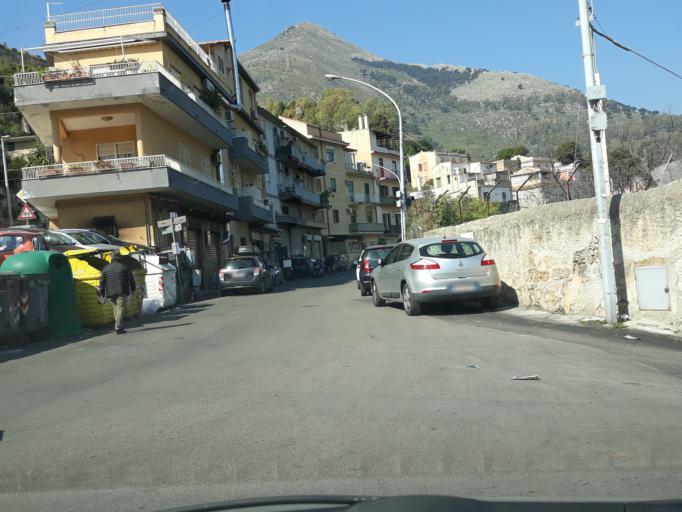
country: IT
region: Sicily
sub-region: Palermo
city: Piano dei Geli
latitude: 38.1142
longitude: 13.2961
